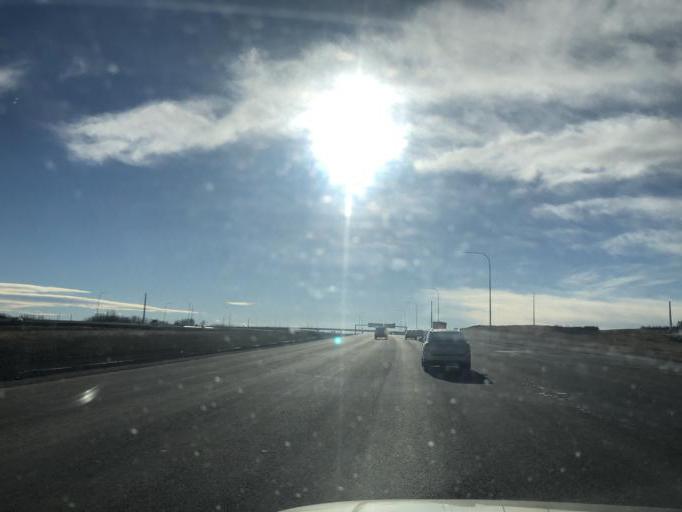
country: CA
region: Alberta
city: Calgary
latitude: 50.9843
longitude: -114.1650
